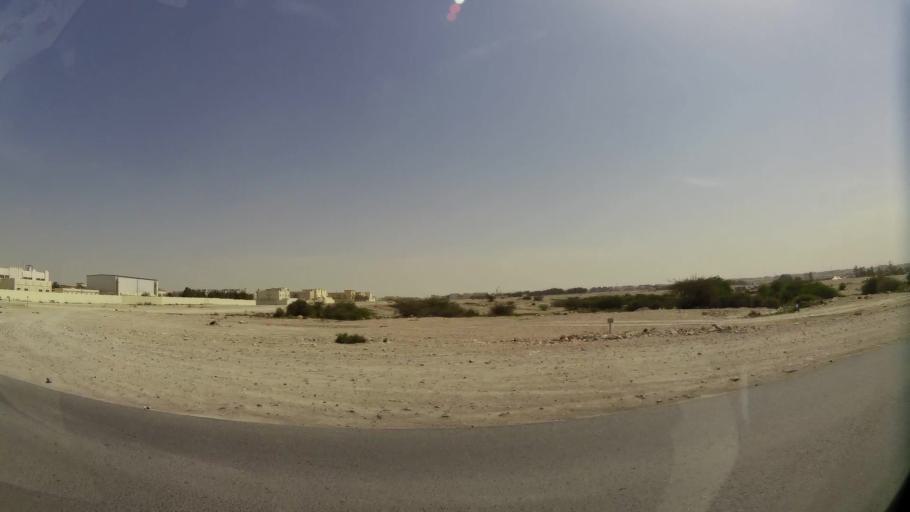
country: QA
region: Baladiyat ar Rayyan
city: Ar Rayyan
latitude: 25.2638
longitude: 51.4051
